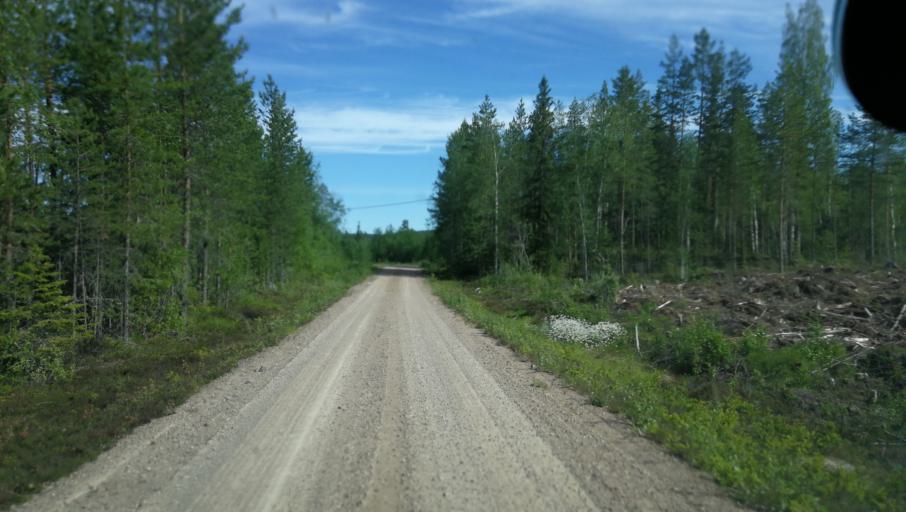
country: SE
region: Dalarna
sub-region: Vansbro Kommun
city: Vansbro
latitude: 60.8327
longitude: 14.1601
